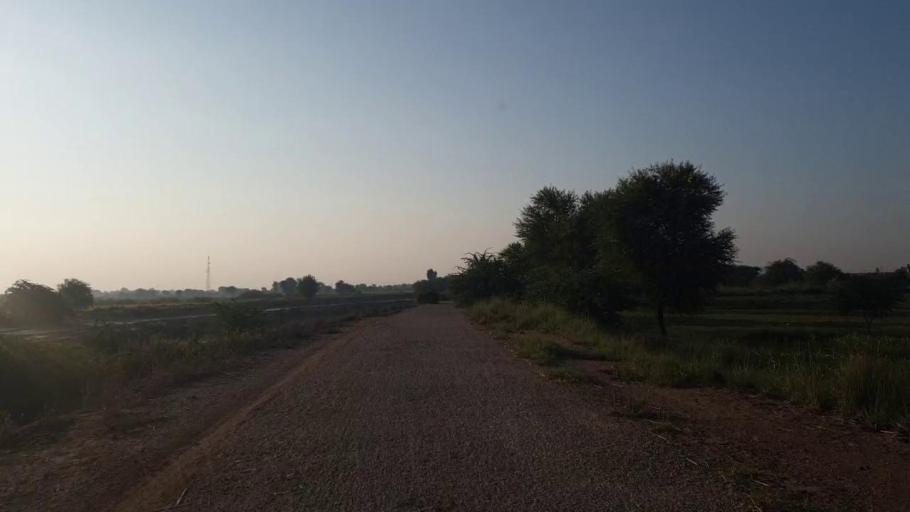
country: PK
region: Sindh
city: Badin
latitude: 24.6547
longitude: 68.7894
